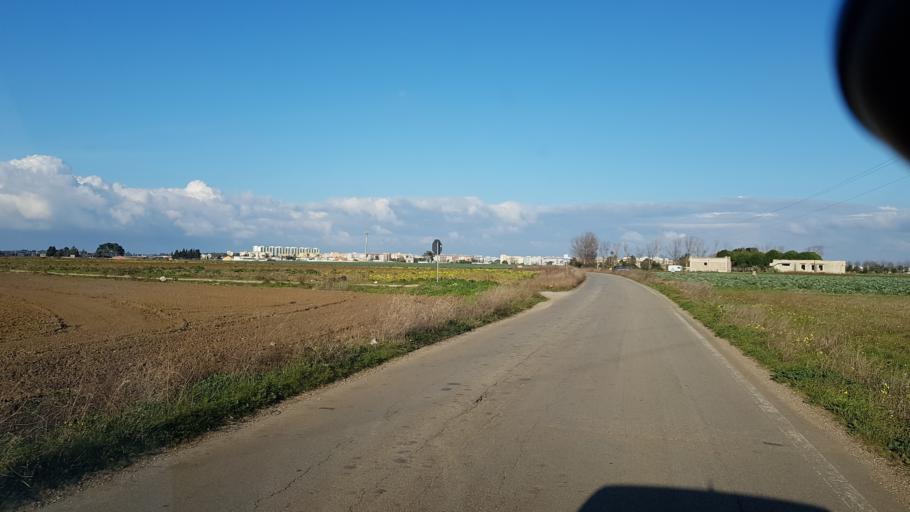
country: IT
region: Apulia
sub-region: Provincia di Brindisi
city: Brindisi
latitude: 40.6058
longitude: 17.9097
